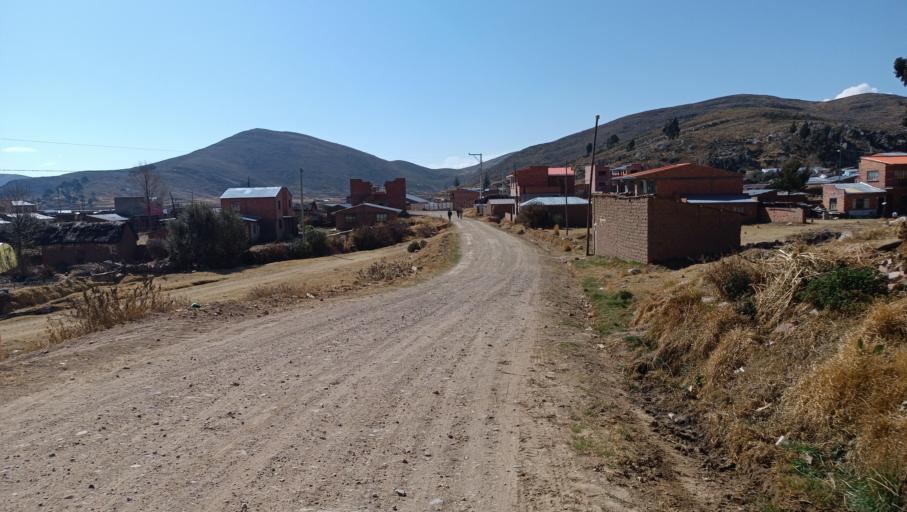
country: BO
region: La Paz
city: Huatajata
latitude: -16.3460
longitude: -68.6750
